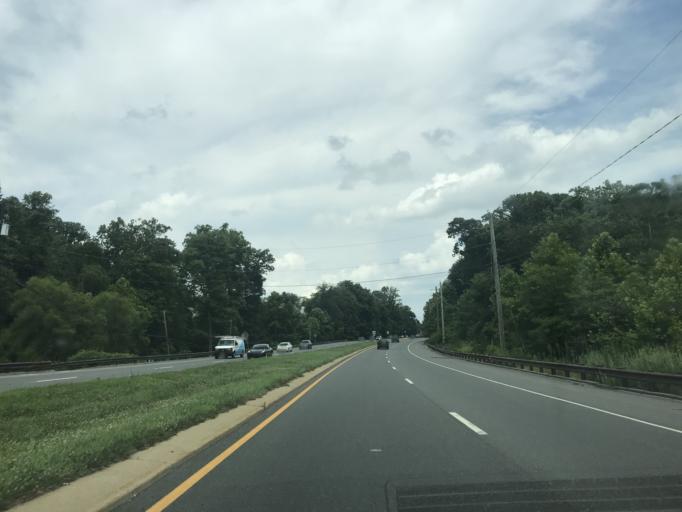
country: US
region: Delaware
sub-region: New Castle County
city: Greenville
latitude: 39.7629
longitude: -75.6348
